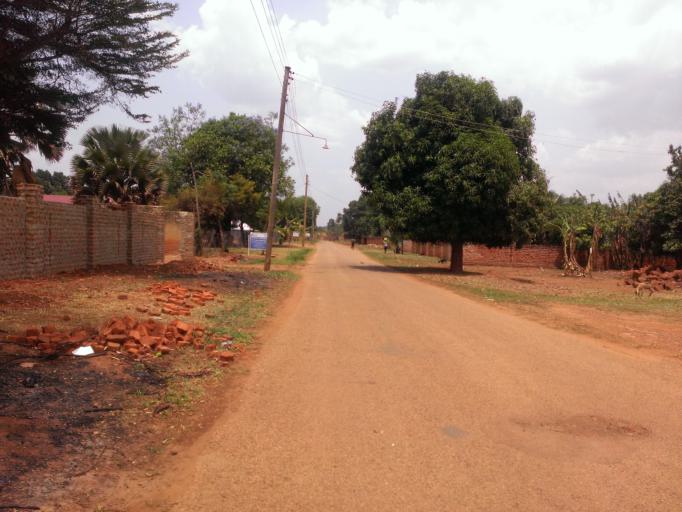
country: UG
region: Northern Region
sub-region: Gulu District
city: Gulu
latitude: 2.7812
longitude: 32.3006
